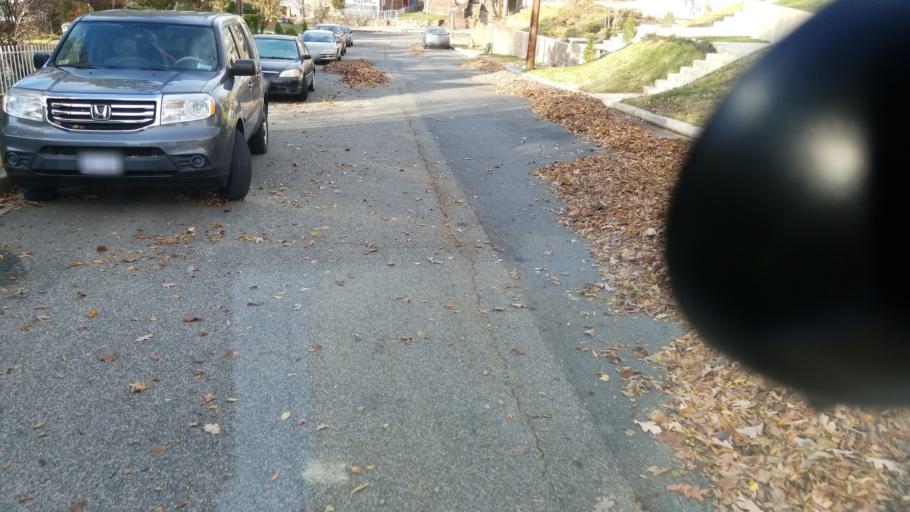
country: US
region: Maryland
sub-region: Prince George's County
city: Silver Hill
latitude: 38.8764
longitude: -76.9597
